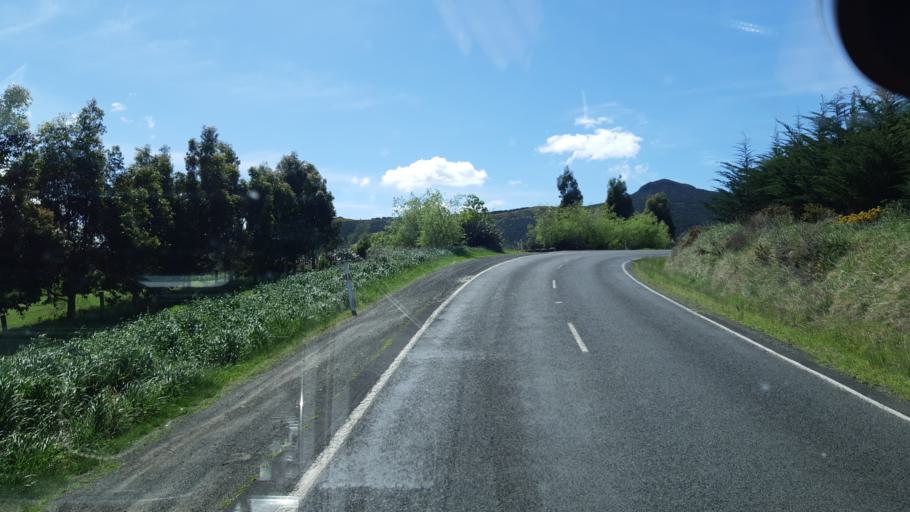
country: NZ
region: Otago
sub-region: Dunedin City
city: Portobello
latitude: -45.7712
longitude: 170.5832
